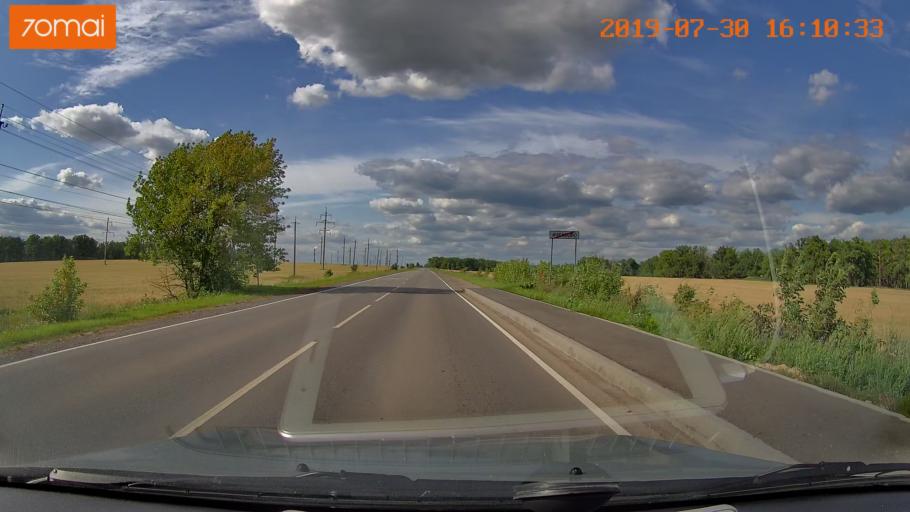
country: RU
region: Moskovskaya
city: Peski
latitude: 55.2640
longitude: 38.7156
